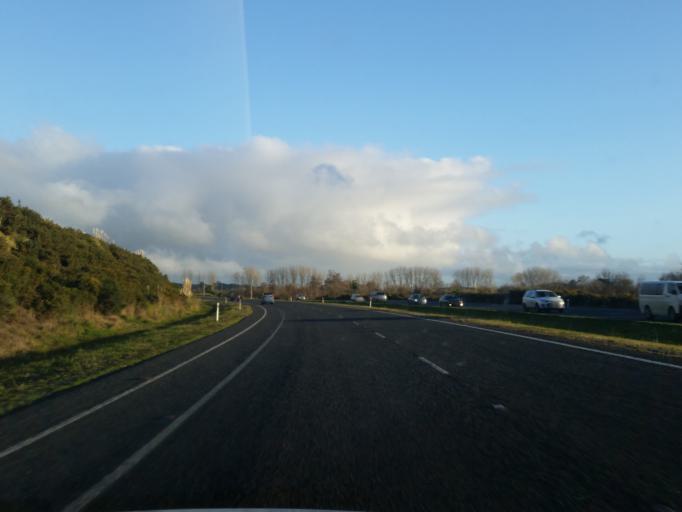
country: NZ
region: Waikato
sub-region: Waikato District
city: Te Kauwhata
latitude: -37.3309
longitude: 175.0635
